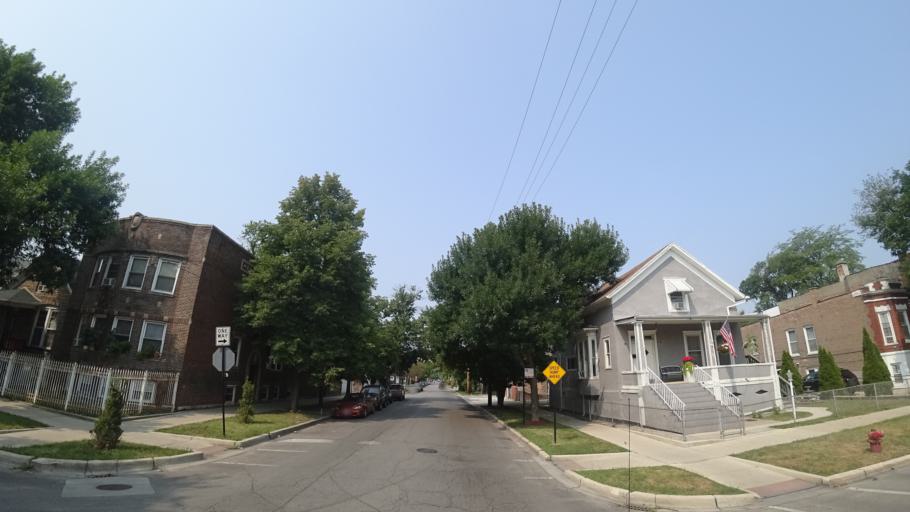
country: US
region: Illinois
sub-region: Cook County
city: Cicero
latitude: 41.8462
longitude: -87.7185
